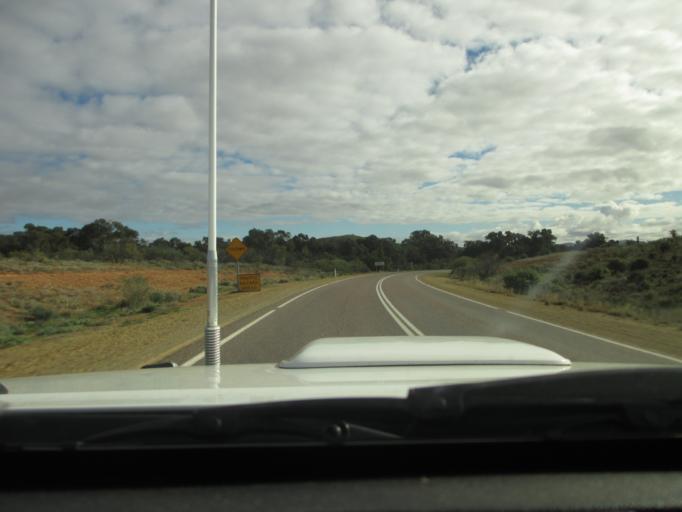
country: AU
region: South Australia
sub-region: Flinders Ranges
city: Quorn
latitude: -32.3341
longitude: 138.4741
